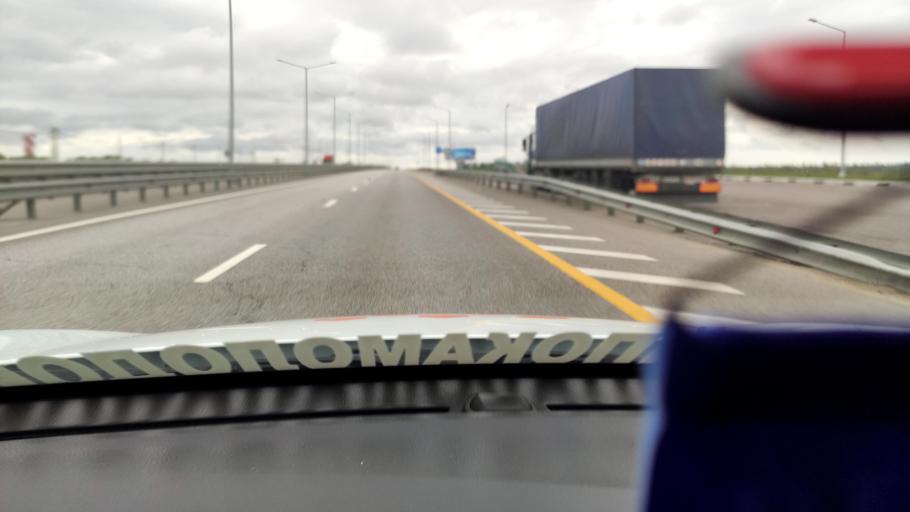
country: RU
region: Voronezj
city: Podkletnoye
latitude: 51.5435
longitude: 39.4984
